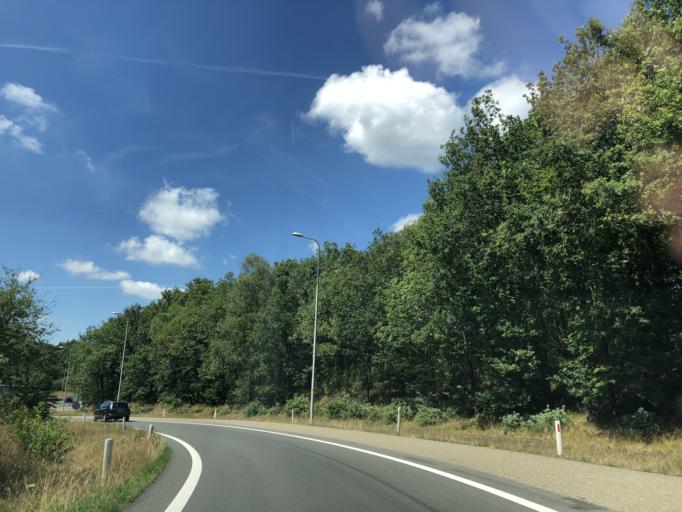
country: NL
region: Gelderland
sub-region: Gemeente Renkum
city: Heelsum
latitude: 51.9759
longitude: 5.7652
